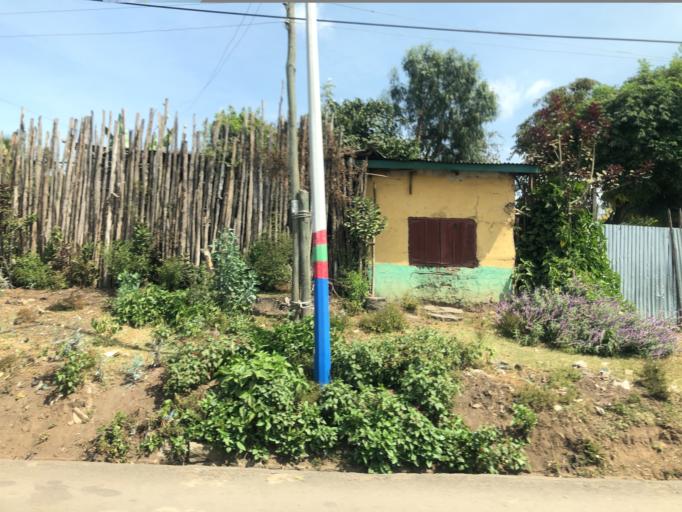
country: ET
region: Oromiya
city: Shashemene
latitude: 7.2689
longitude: 38.6563
